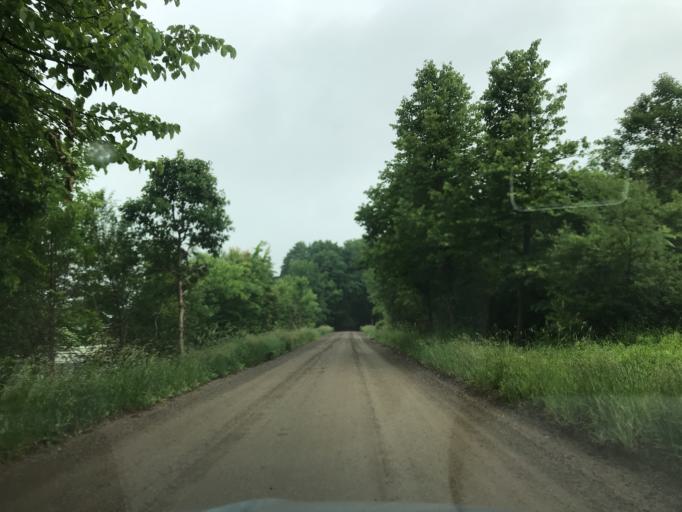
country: US
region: Michigan
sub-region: Oakland County
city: South Lyon
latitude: 42.4937
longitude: -83.5948
